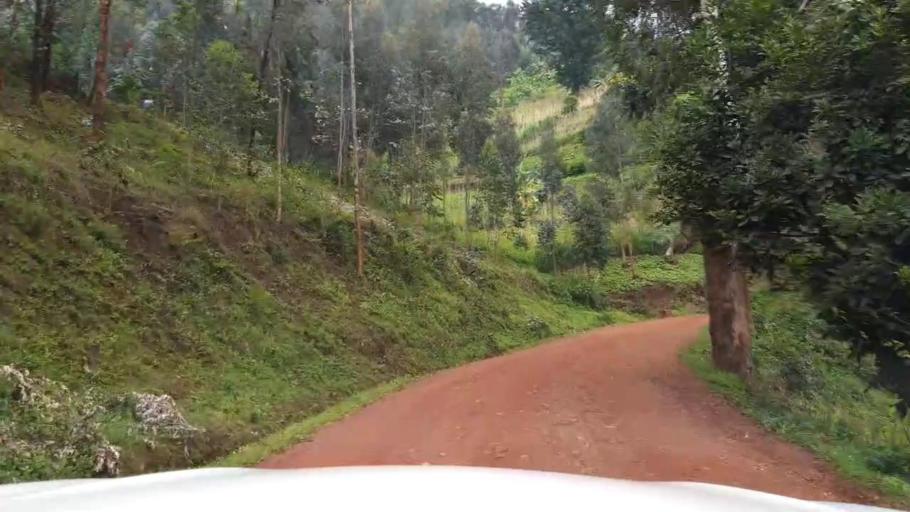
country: UG
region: Western Region
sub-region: Kisoro District
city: Kisoro
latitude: -1.3867
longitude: 29.7984
